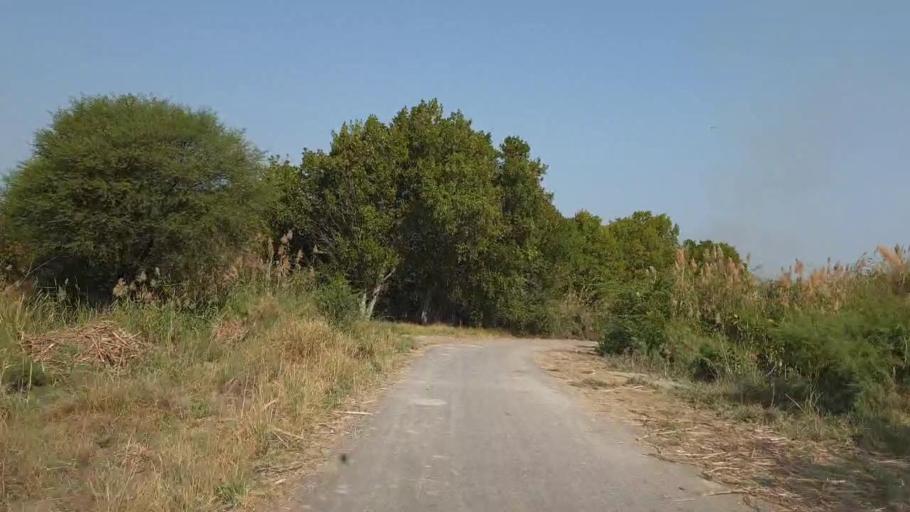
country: PK
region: Sindh
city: Mirpur Khas
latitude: 25.5919
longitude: 69.0020
